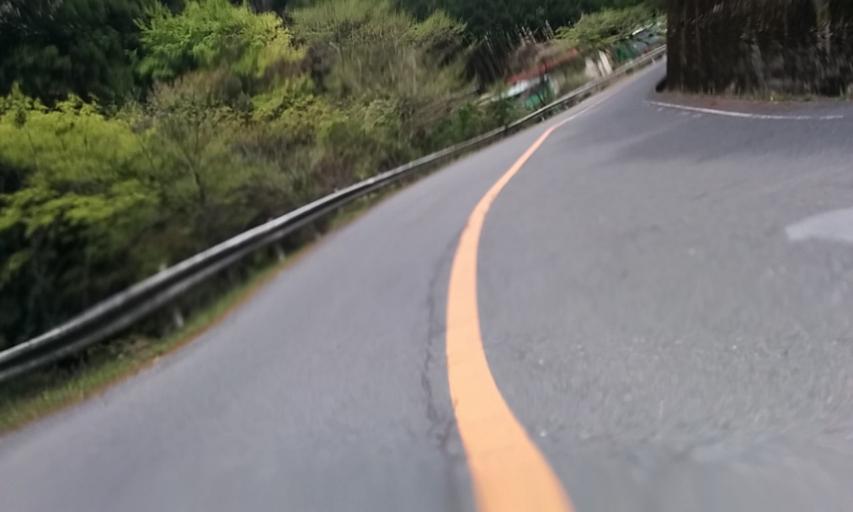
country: JP
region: Kyoto
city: Kameoka
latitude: 34.9365
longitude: 135.6003
